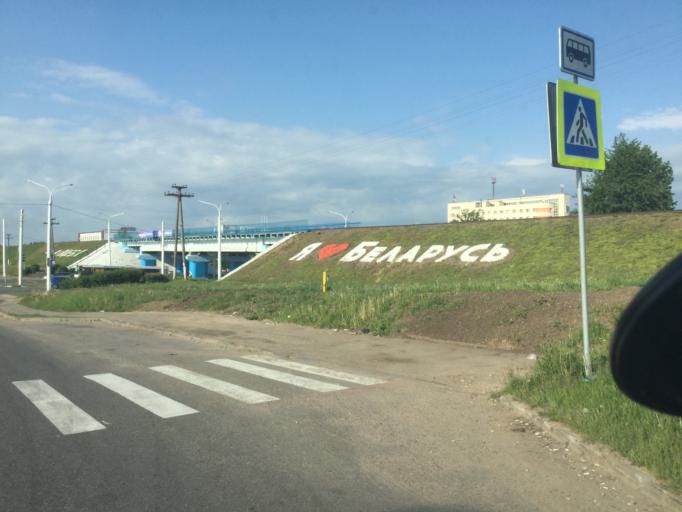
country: BY
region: Vitebsk
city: Vitebsk
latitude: 55.1763
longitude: 30.2501
